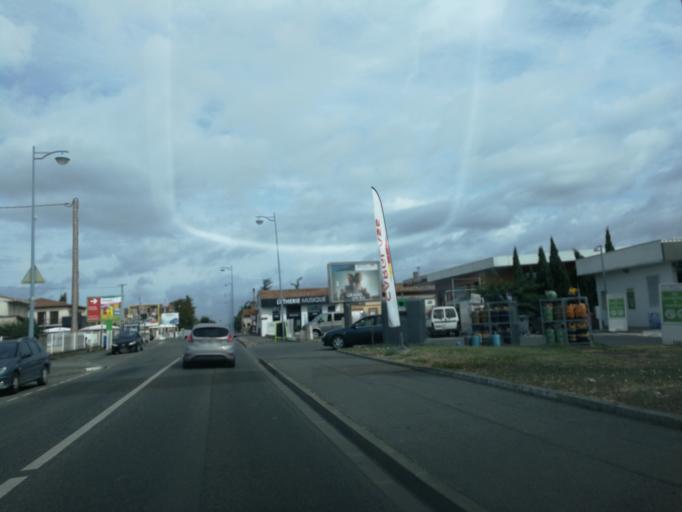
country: FR
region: Midi-Pyrenees
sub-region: Departement de la Haute-Garonne
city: Saint-Alban
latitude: 43.6833
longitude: 1.4201
